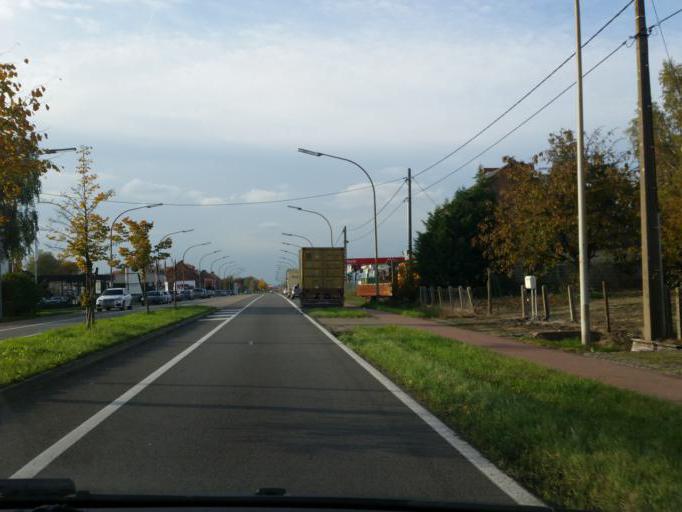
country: BE
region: Flanders
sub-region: Provincie Antwerpen
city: Putte
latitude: 51.0869
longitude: 4.6420
